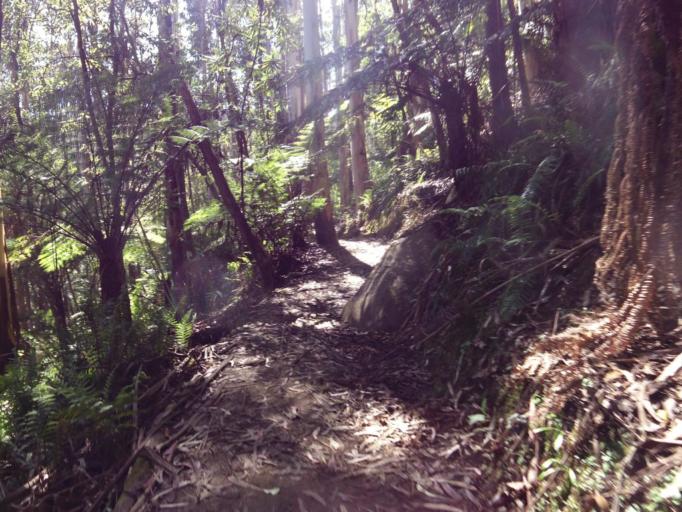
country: AU
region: Victoria
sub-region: Baw Baw
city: Warragul
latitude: -37.8477
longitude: 146.0495
